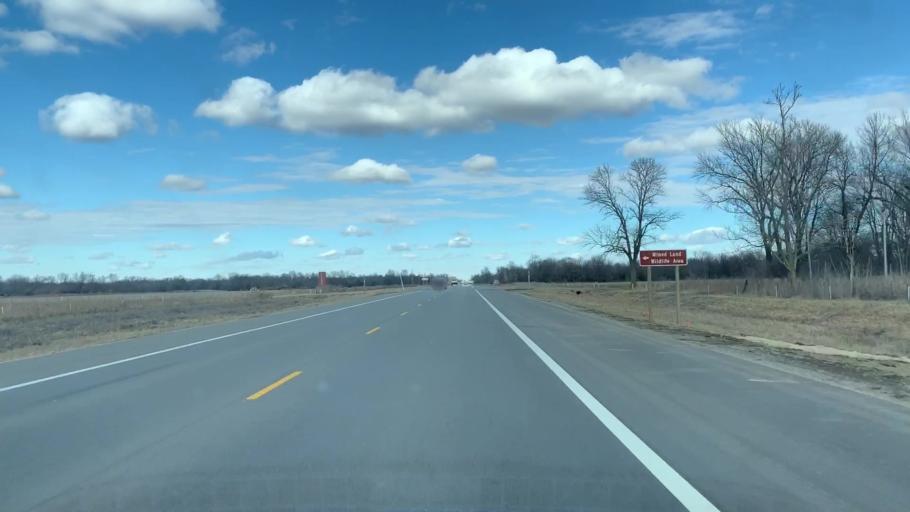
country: US
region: Kansas
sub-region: Cherokee County
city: Columbus
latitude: 37.2658
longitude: -94.8318
